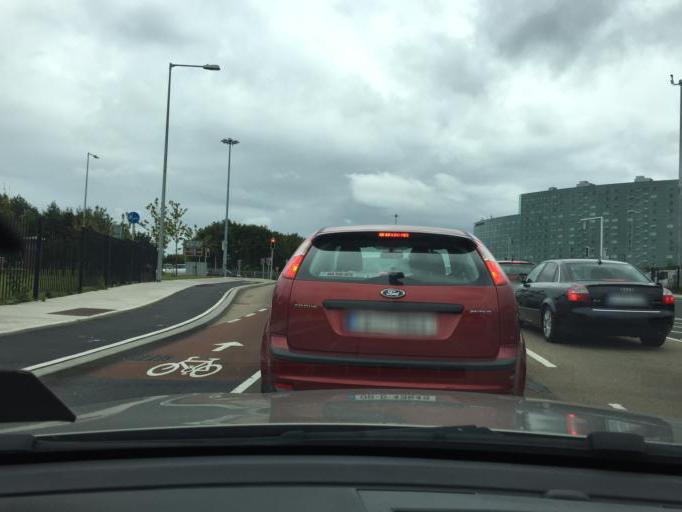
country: IE
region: Leinster
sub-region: Fingal County
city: Blanchardstown
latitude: 53.3985
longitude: -6.3911
